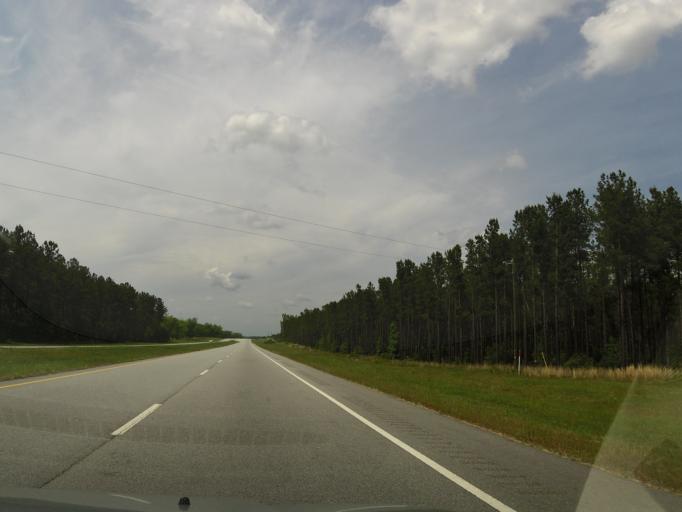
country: US
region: Georgia
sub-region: Jefferson County
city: Wadley
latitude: 32.7918
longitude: -82.3965
